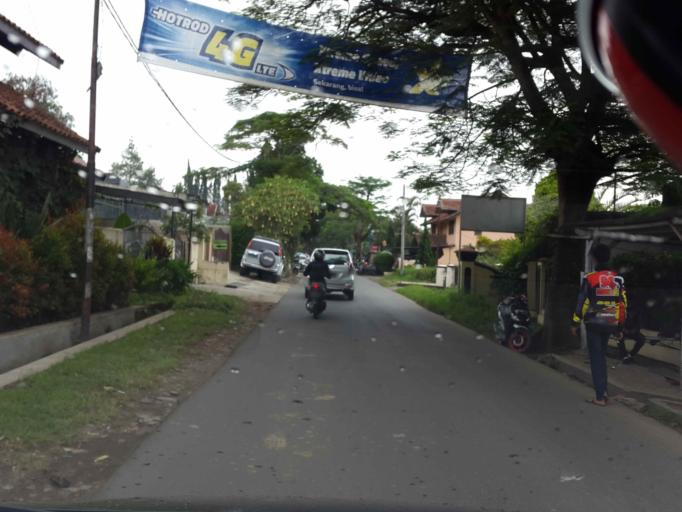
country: ID
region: West Java
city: Lembang
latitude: -6.8188
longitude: 107.6328
